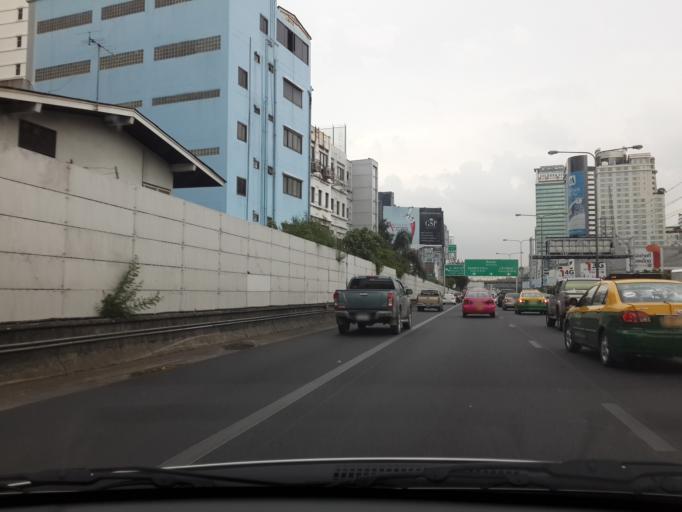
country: TH
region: Bangkok
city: Pathum Wan
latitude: 13.7370
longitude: 100.5511
